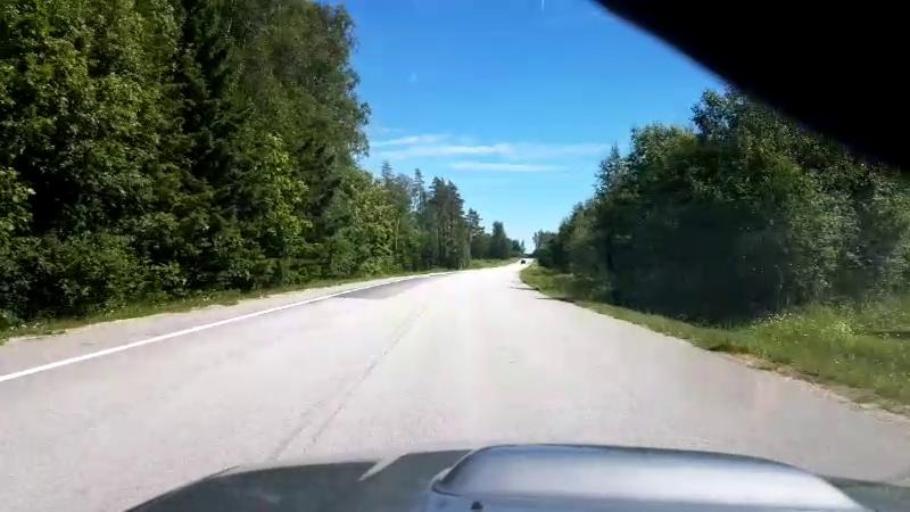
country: EE
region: Jaervamaa
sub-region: Jaerva-Jaani vald
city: Jarva-Jaani
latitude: 58.9959
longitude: 25.9490
